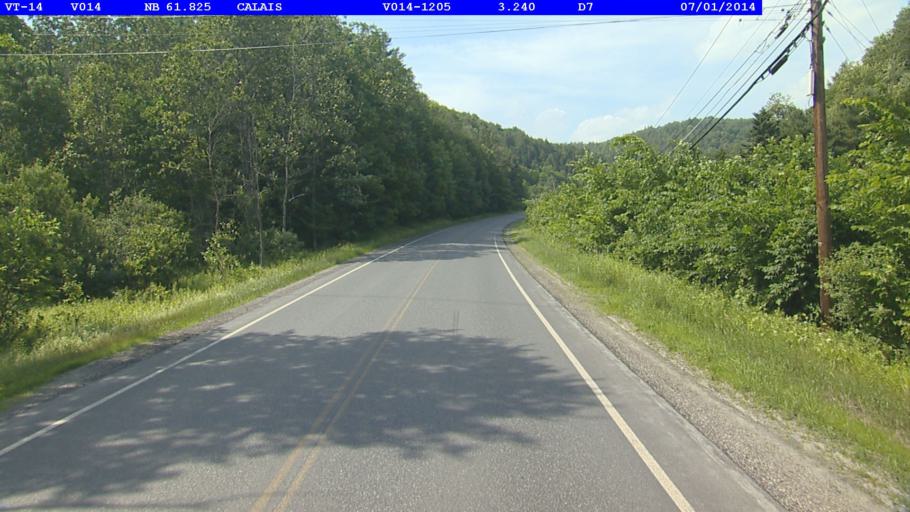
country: US
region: Vermont
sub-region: Washington County
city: Montpelier
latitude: 44.3527
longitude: -72.4436
